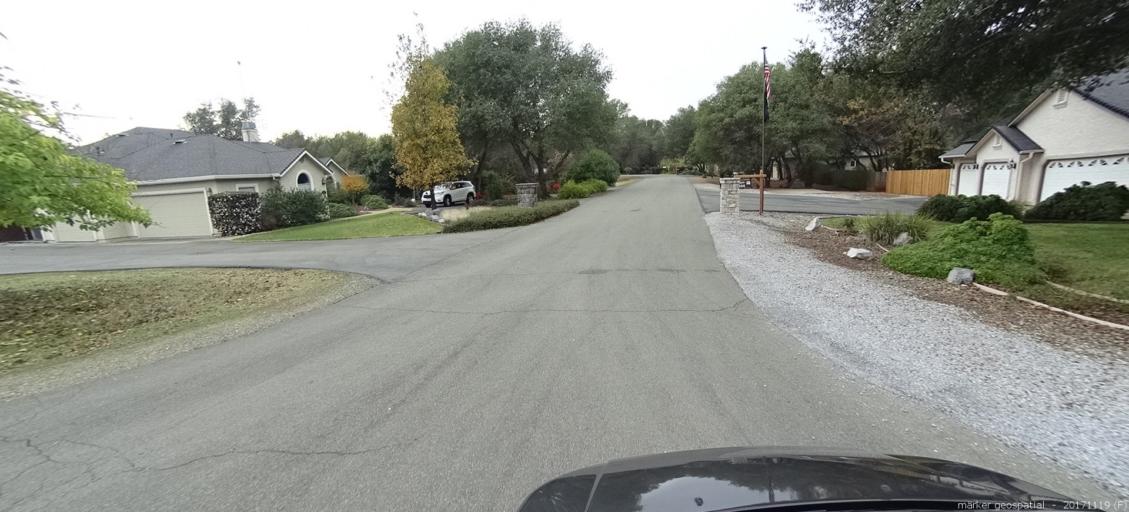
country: US
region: California
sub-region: Shasta County
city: Redding
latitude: 40.4946
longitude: -122.4058
